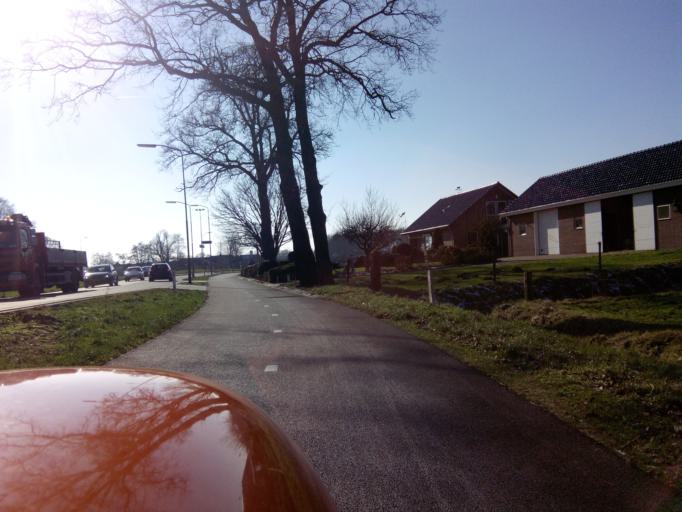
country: NL
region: Gelderland
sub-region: Gemeente Barneveld
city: Barneveld
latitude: 52.1200
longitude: 5.5417
